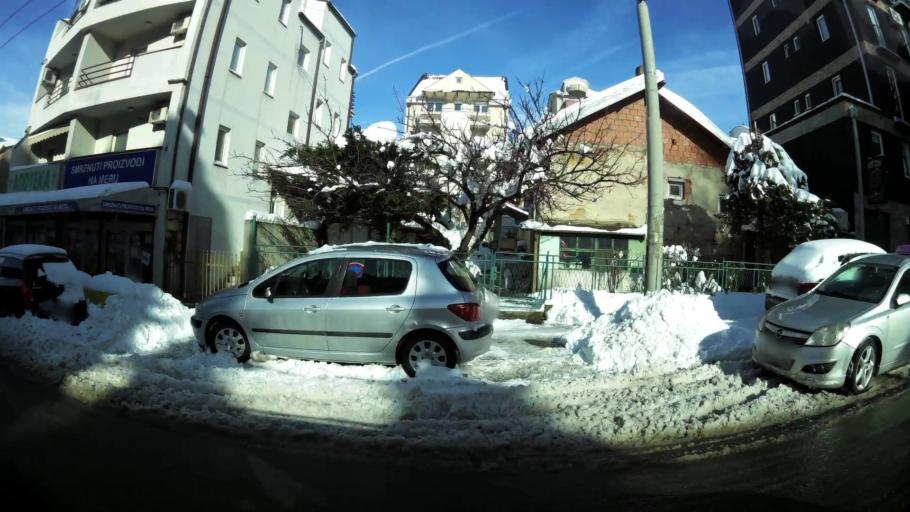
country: RS
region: Central Serbia
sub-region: Belgrade
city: Palilula
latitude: 44.7886
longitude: 20.5079
